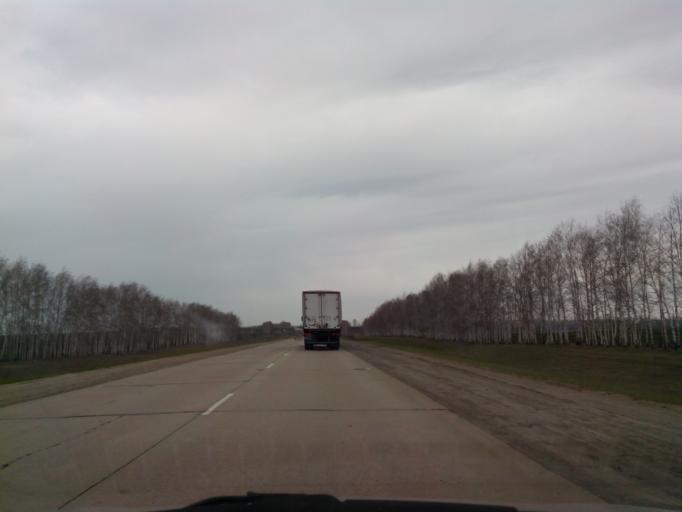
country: RU
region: Tambov
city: Pokrovo-Prigorodnoye
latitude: 52.6514
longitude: 41.3406
